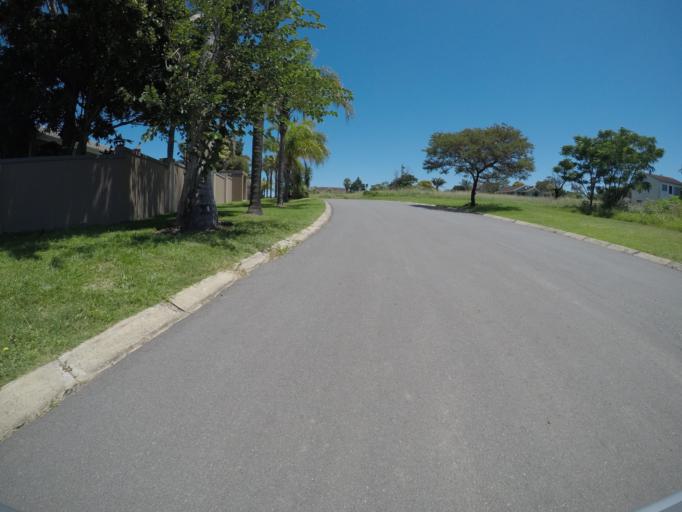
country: ZA
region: Eastern Cape
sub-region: Buffalo City Metropolitan Municipality
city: East London
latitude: -32.9529
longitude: 27.9377
